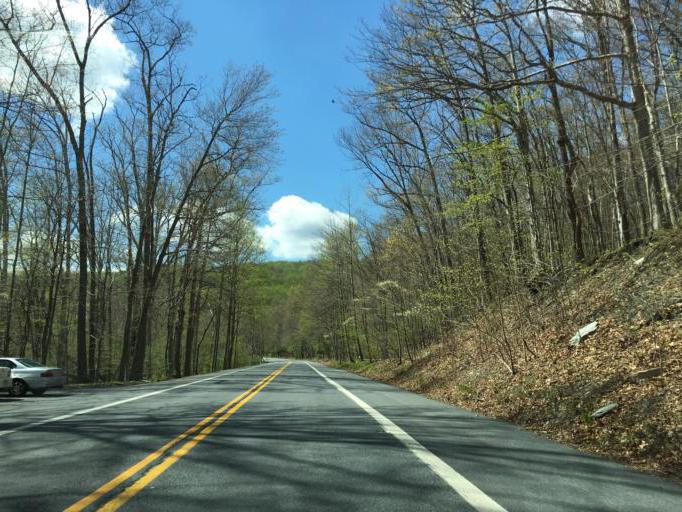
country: US
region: Maryland
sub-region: Frederick County
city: Thurmont
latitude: 39.6325
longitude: -77.4469
